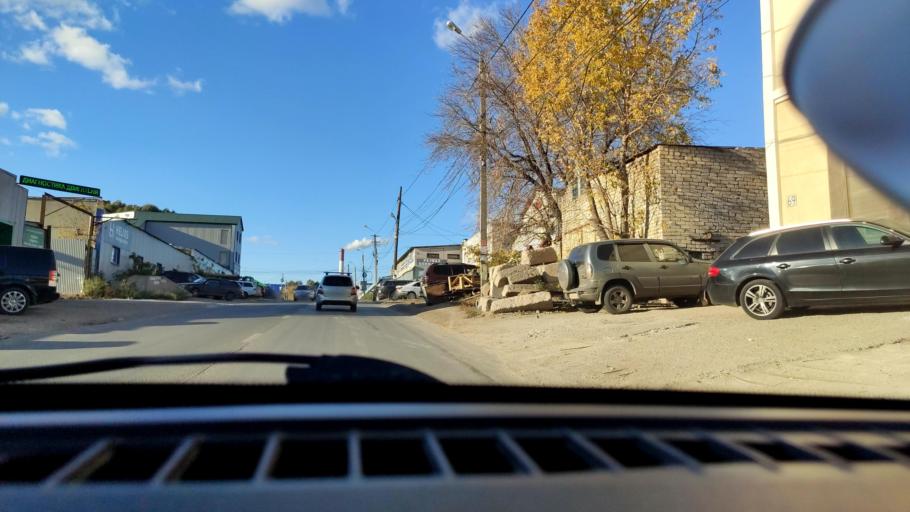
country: RU
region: Samara
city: Samara
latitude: 53.1788
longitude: 50.1681
